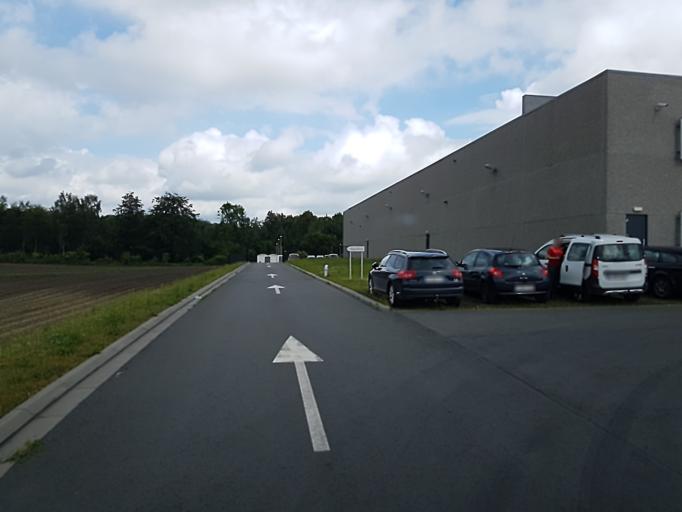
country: BE
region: Wallonia
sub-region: Province du Hainaut
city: Jurbise
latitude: 50.4869
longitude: 3.8968
